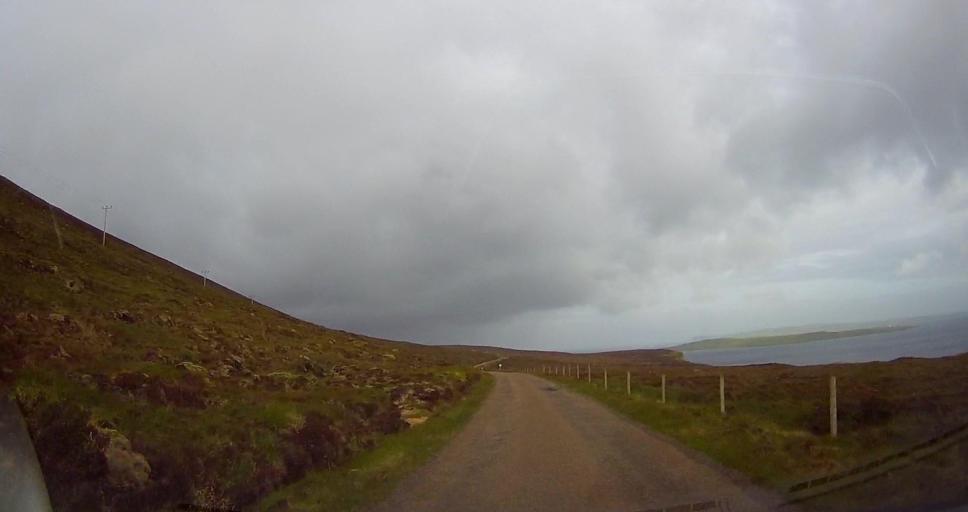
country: GB
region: Scotland
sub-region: Orkney Islands
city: Stromness
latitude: 58.8893
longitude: -3.2555
